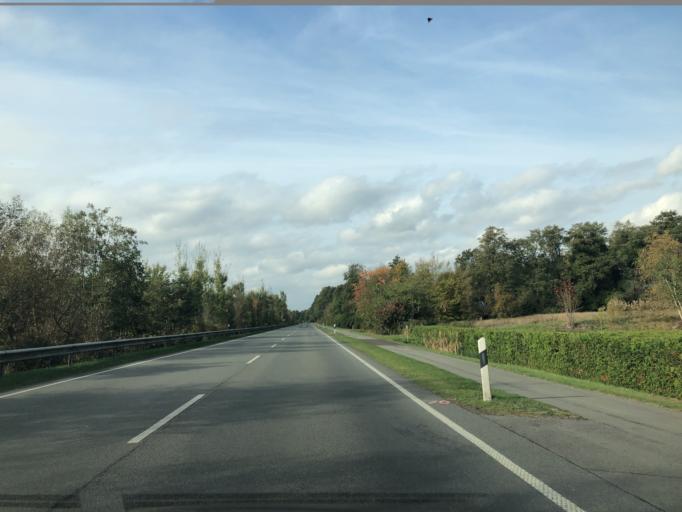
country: DE
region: Lower Saxony
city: Edewecht
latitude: 53.0905
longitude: 7.9173
